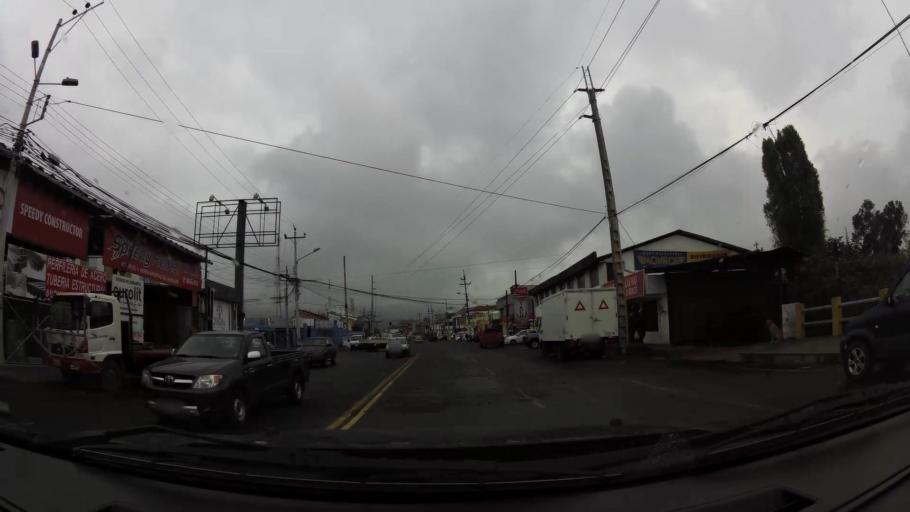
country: EC
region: Pichincha
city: Sangolqui
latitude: -0.2986
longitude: -78.4571
